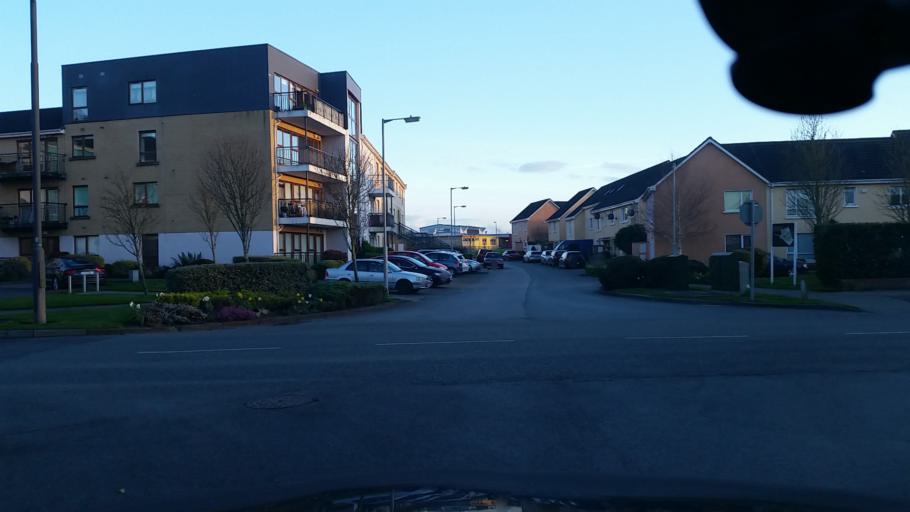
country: IE
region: Leinster
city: Hartstown
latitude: 53.3960
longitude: -6.4414
